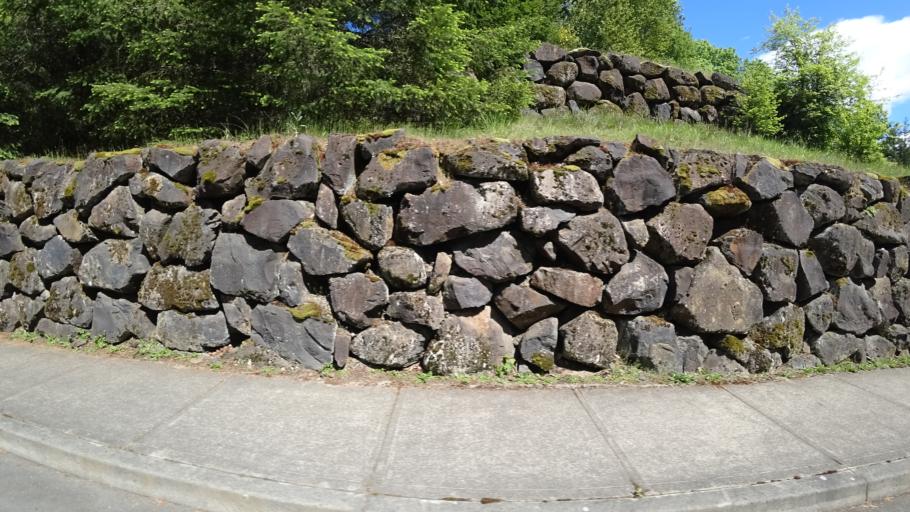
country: US
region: Oregon
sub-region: Washington County
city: West Haven
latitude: 45.5480
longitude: -122.7741
